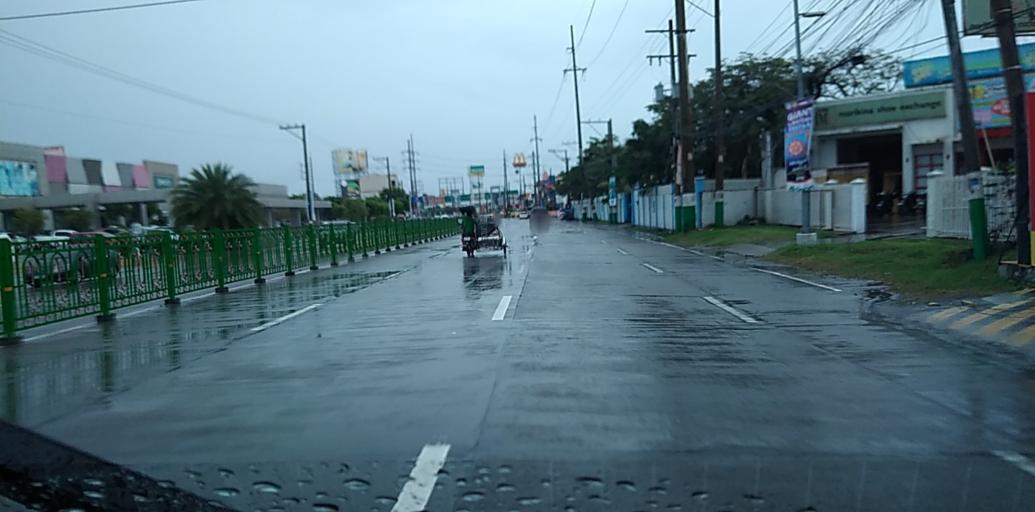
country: PH
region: Central Luzon
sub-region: Province of Pampanga
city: Del Pilar
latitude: 15.0513
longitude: 120.7011
